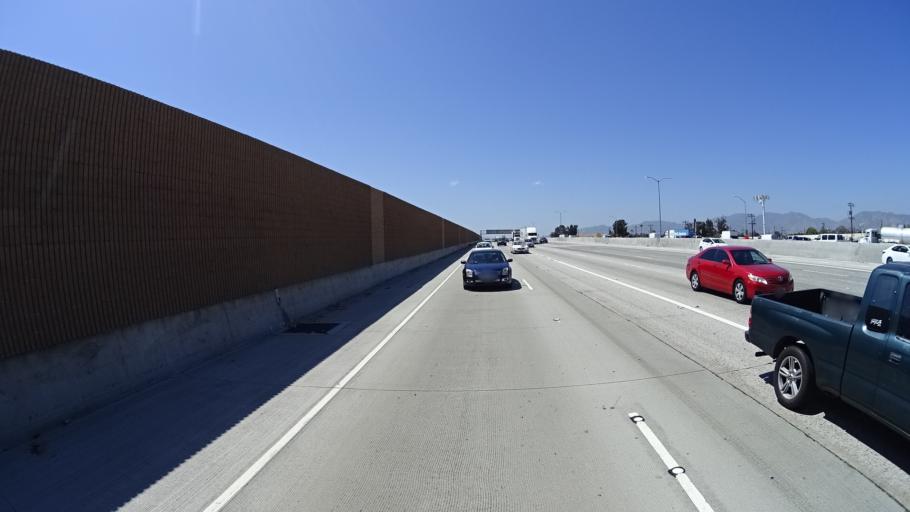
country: US
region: California
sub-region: Los Angeles County
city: San Fernando
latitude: 34.2369
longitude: -118.4145
